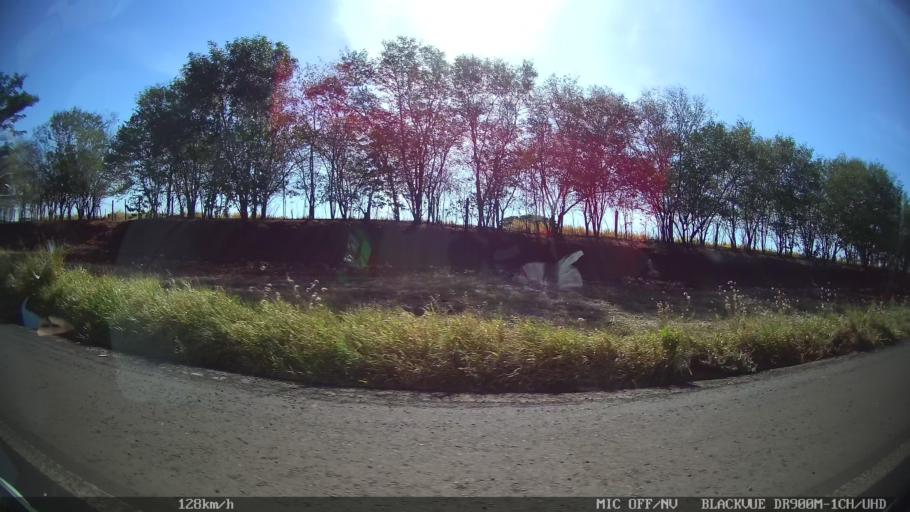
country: BR
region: Sao Paulo
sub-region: Barretos
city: Barretos
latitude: -20.5812
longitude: -48.6904
